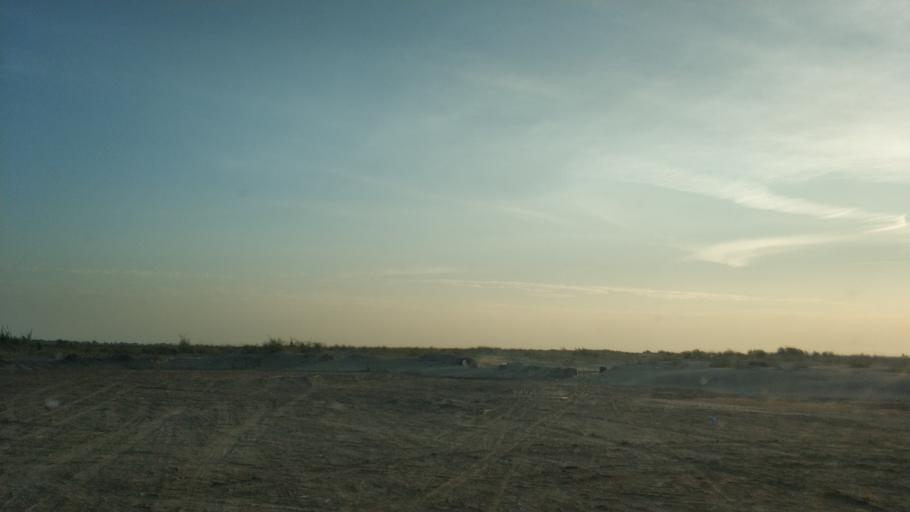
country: AL
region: Fier
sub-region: Rrethi i Lushnjes
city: Divjake
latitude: 40.9571
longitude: 19.4681
